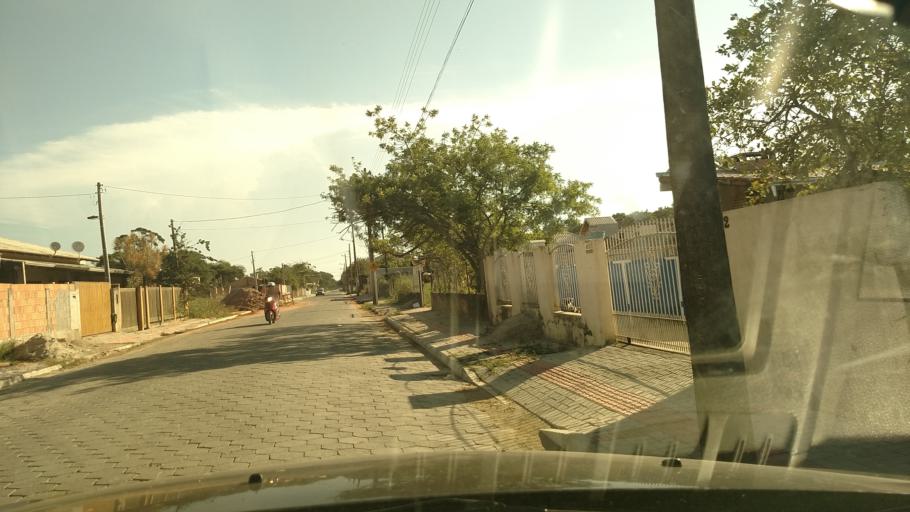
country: BR
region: Santa Catarina
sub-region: Porto Belo
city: Porto Belo
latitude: -27.1771
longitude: -48.5064
